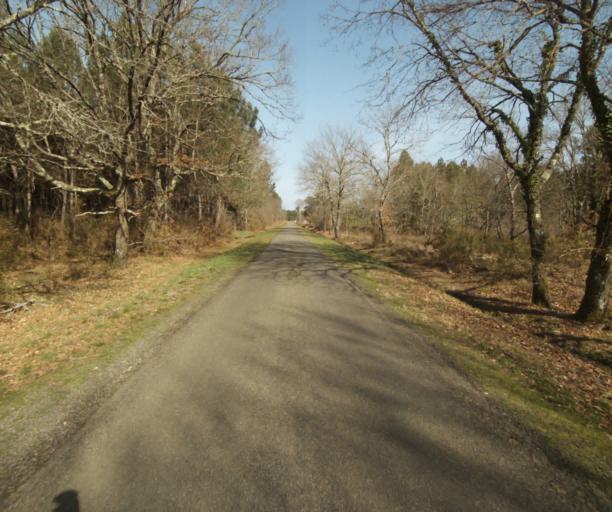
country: FR
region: Aquitaine
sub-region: Departement des Landes
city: Roquefort
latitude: 44.1549
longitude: -0.2285
